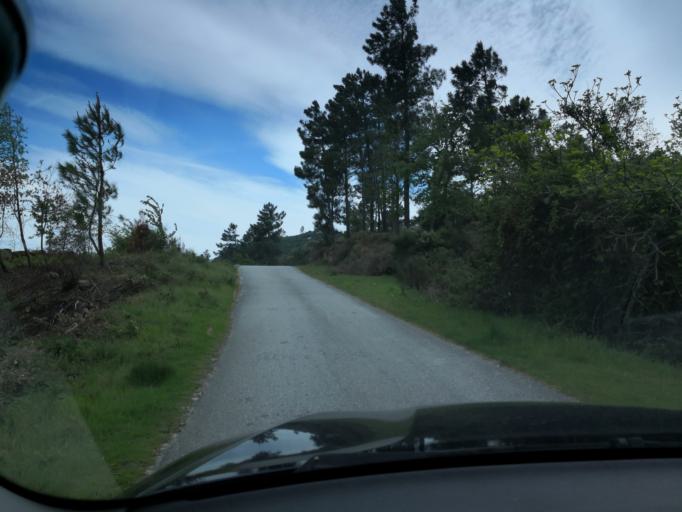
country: PT
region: Vila Real
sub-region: Vila Real
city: Vila Real
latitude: 41.3012
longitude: -7.8035
